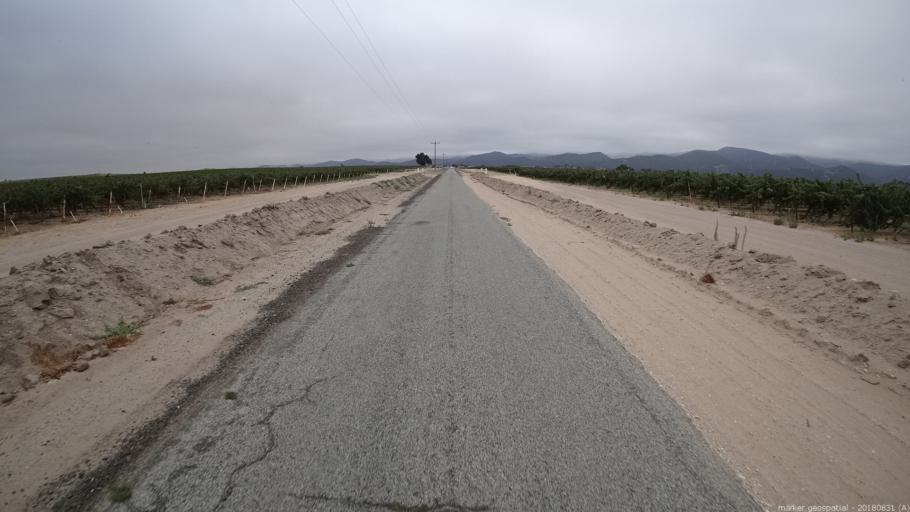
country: US
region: California
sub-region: Monterey County
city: King City
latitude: 36.1189
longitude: -121.0874
